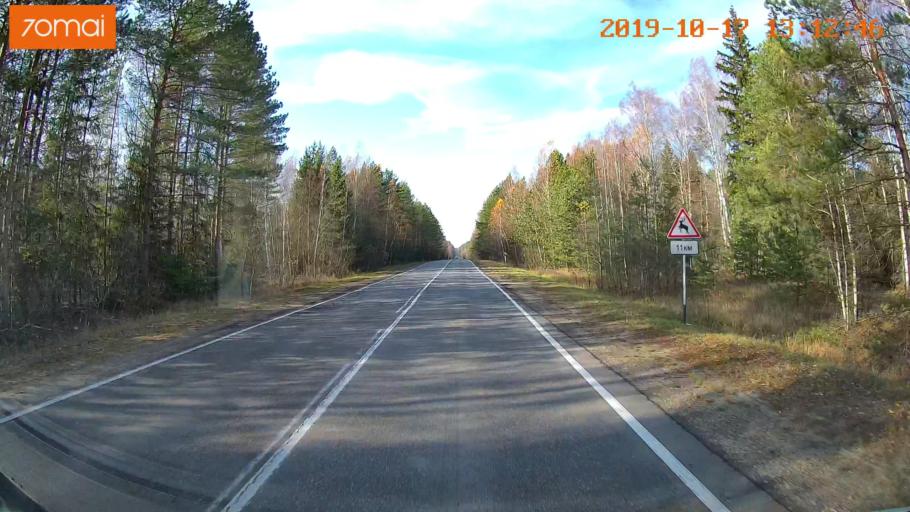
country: RU
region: Rjazan
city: Gus'-Zheleznyy
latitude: 55.0393
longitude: 41.2056
